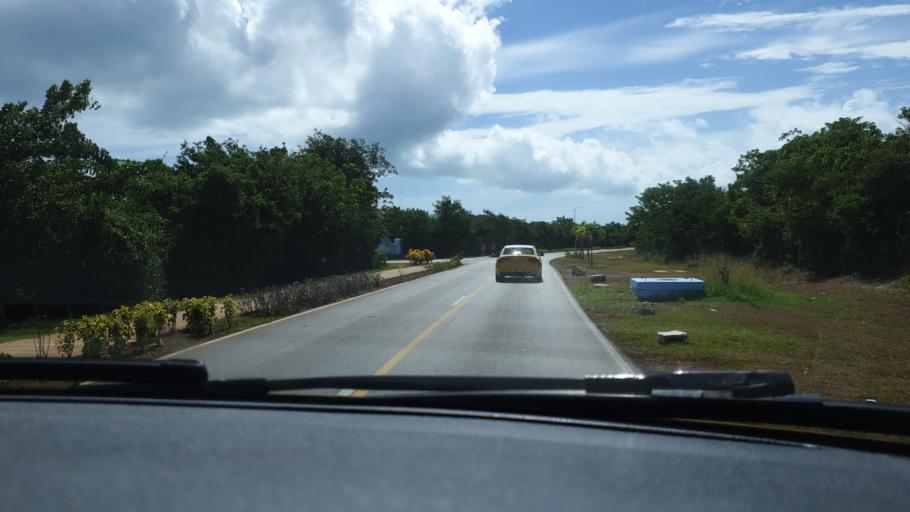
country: CU
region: Sancti Spiritus
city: Yaguajay
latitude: 22.6561
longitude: -79.0359
